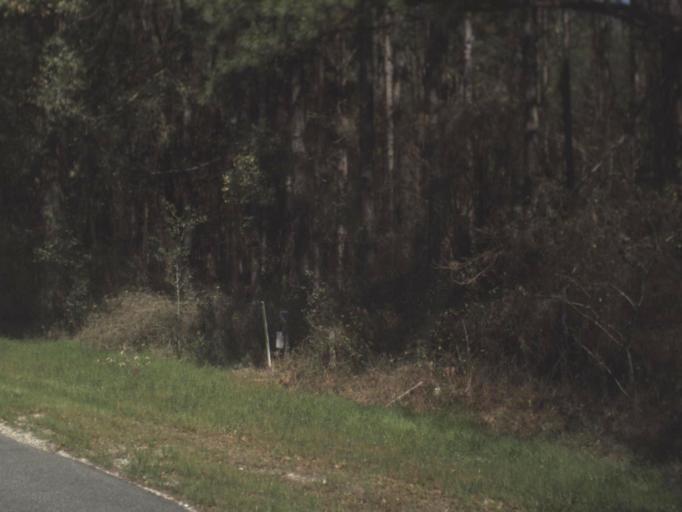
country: US
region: Florida
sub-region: Leon County
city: Woodville
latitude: 30.3051
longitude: -84.2456
